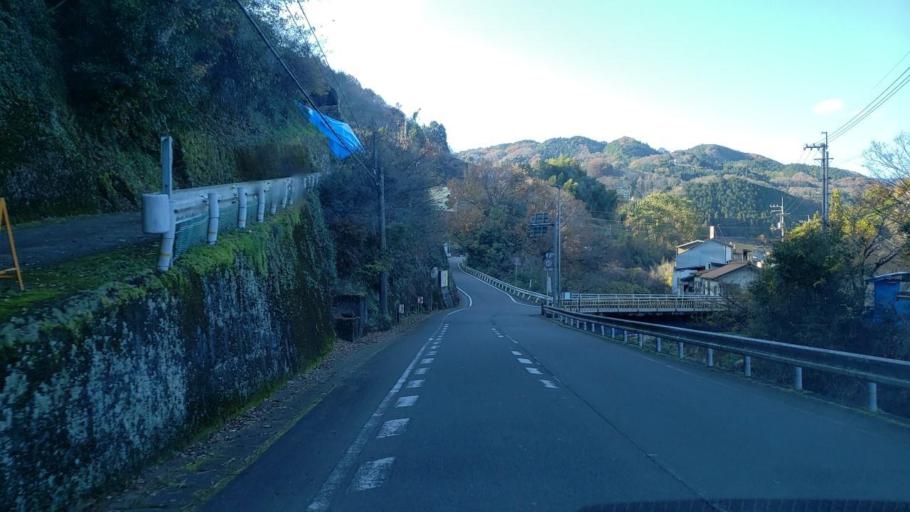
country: JP
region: Tokushima
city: Wakimachi
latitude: 34.0213
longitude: 134.0330
